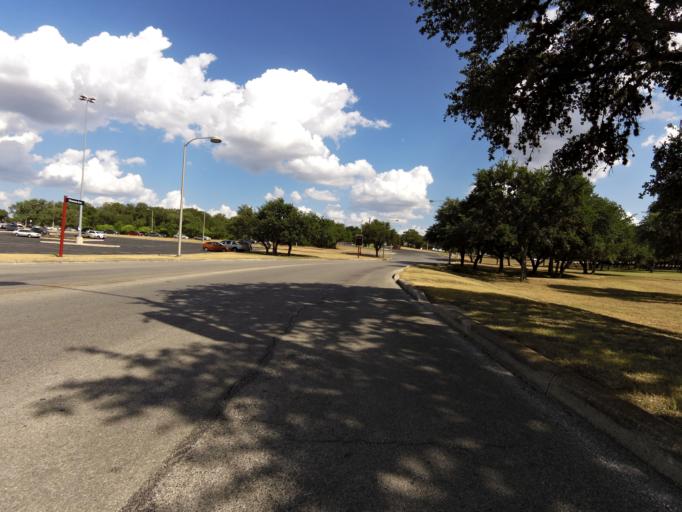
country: US
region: Texas
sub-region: Bexar County
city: Shavano Park
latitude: 29.5804
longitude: -98.6191
